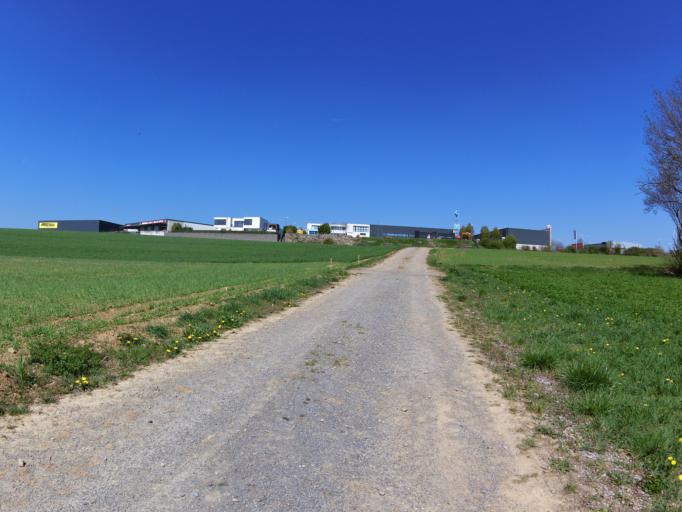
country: DE
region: Bavaria
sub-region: Regierungsbezirk Unterfranken
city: Biebelried
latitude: 49.7756
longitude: 10.0668
